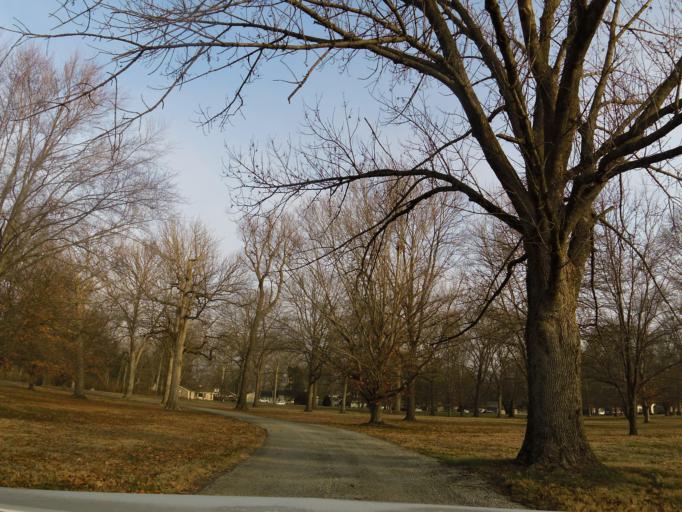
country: US
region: Indiana
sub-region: Bartholomew County
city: Columbus
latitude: 39.2292
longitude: -85.9137
